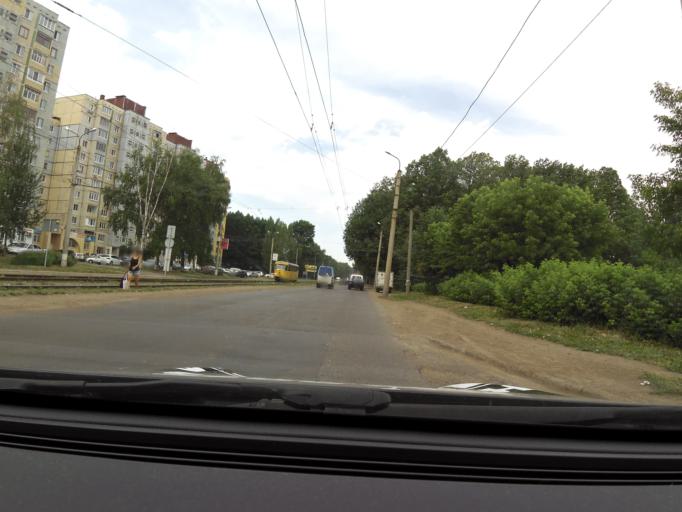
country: RU
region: Bashkortostan
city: Ufa
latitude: 54.7970
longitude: 56.0560
